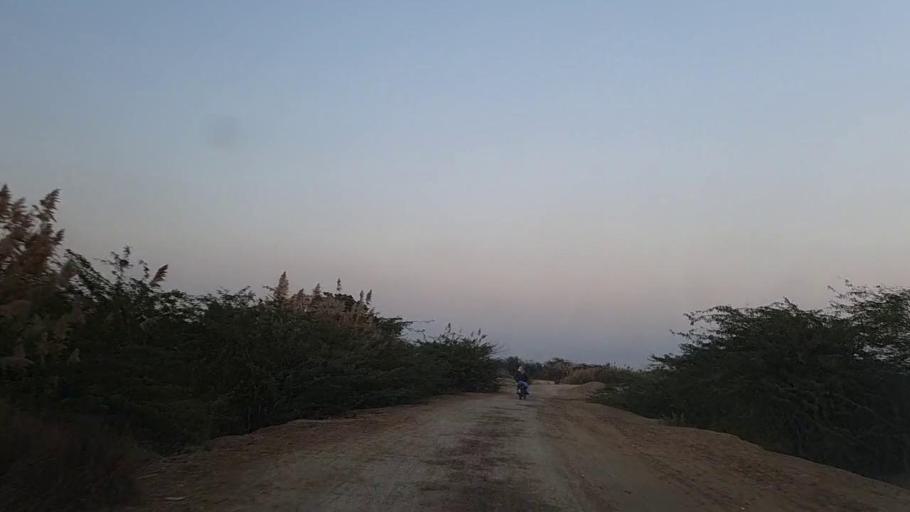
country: PK
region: Sindh
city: Bandhi
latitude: 26.6031
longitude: 68.3656
